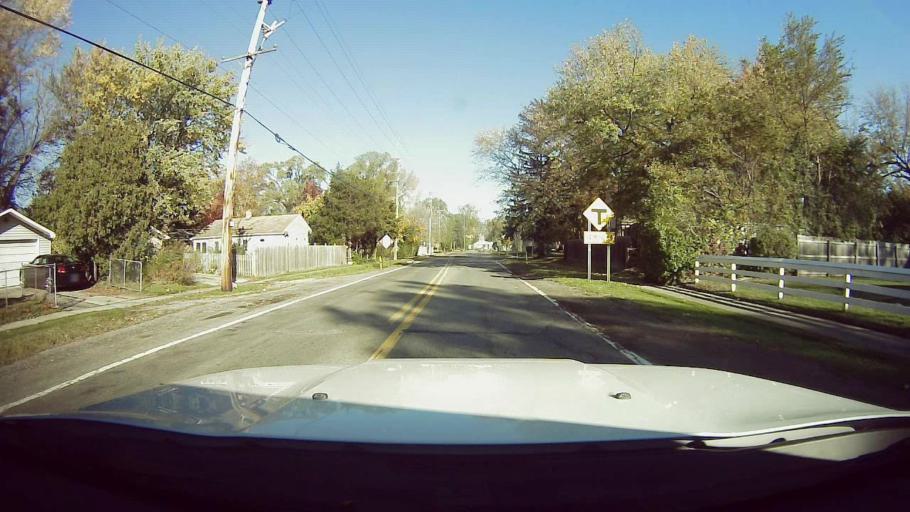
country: US
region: Michigan
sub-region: Oakland County
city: Birmingham
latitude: 42.5305
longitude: -83.2043
